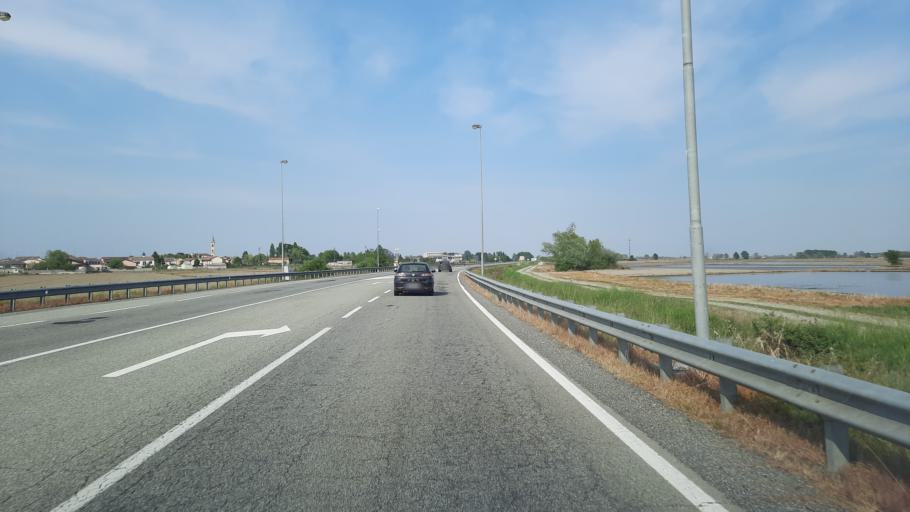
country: IT
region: Piedmont
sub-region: Provincia di Vercelli
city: Desana
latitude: 45.2602
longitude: 8.3512
